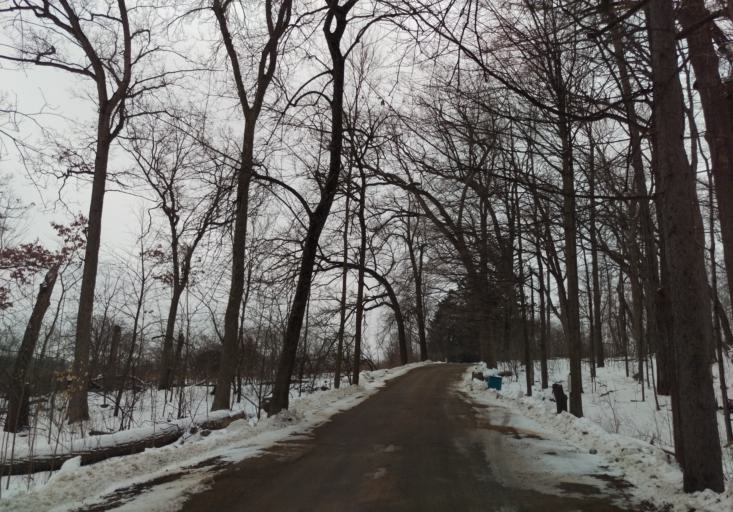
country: US
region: Wisconsin
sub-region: Dane County
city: Middleton
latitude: 43.0743
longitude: -89.4858
